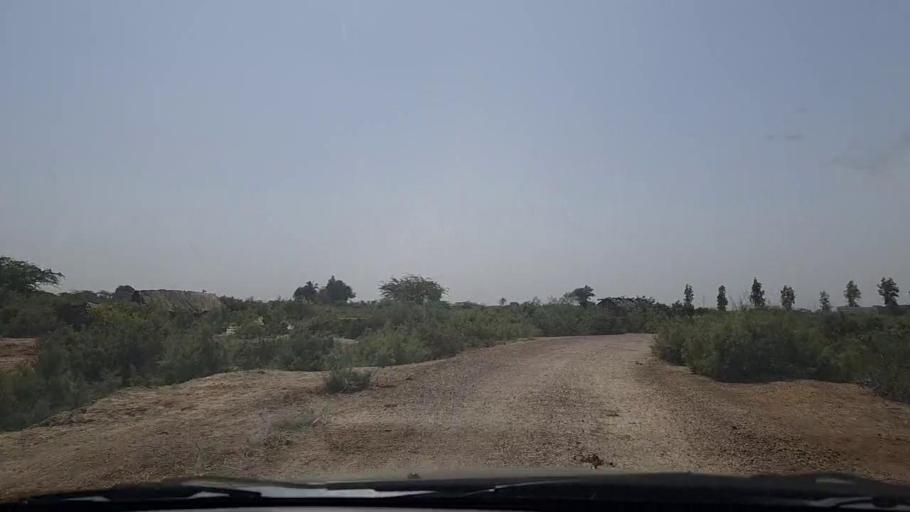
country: PK
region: Sindh
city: Mirpur Sakro
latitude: 24.3204
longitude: 67.6835
